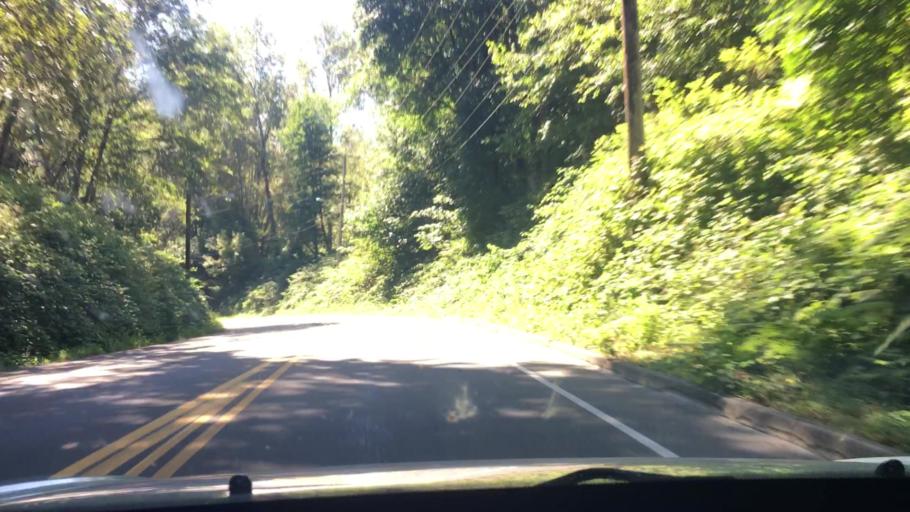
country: US
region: Washington
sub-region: King County
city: Newcastle
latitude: 47.5356
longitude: -122.1318
